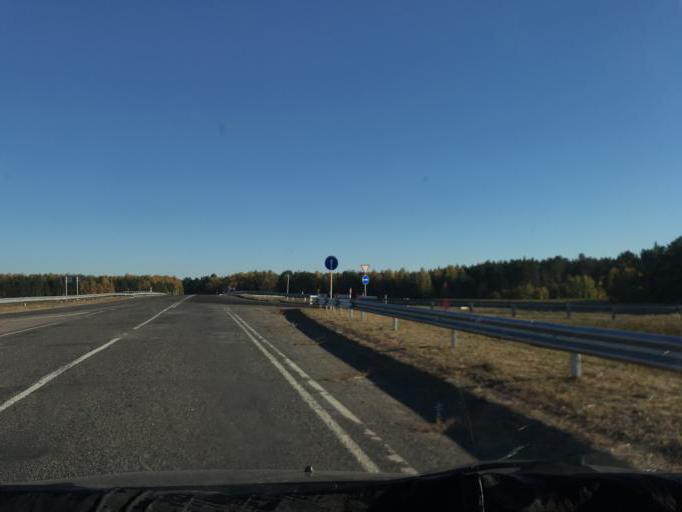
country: BY
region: Gomel
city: Kalinkavichy
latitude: 52.0738
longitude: 29.3592
